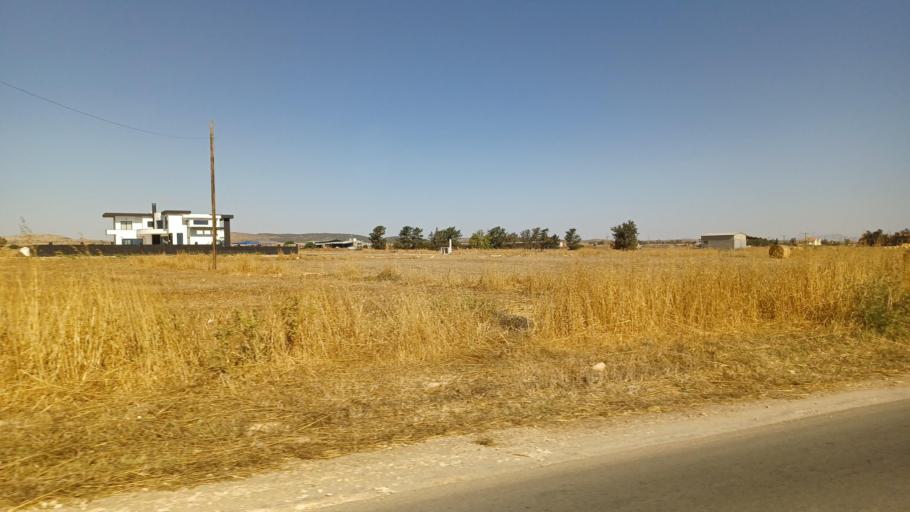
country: CY
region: Larnaka
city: Pergamos
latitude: 35.0313
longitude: 33.7053
